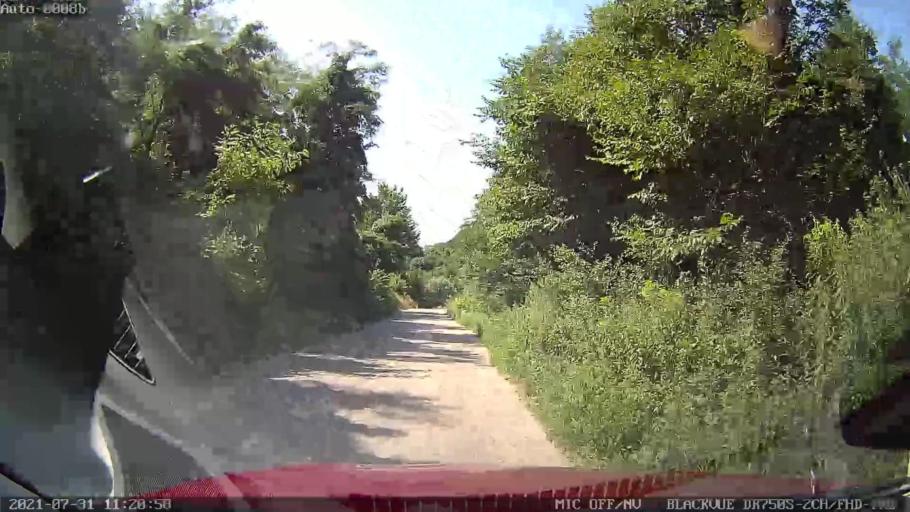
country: HR
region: Varazdinska
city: Jalzabet
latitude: 46.2303
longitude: 16.4751
